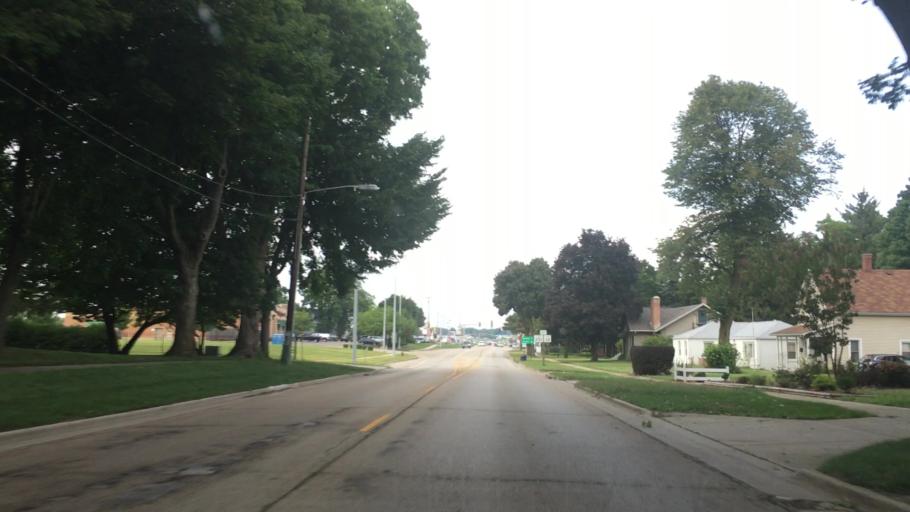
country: US
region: Illinois
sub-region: Ogle County
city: Rochelle
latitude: 41.9314
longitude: -89.0684
